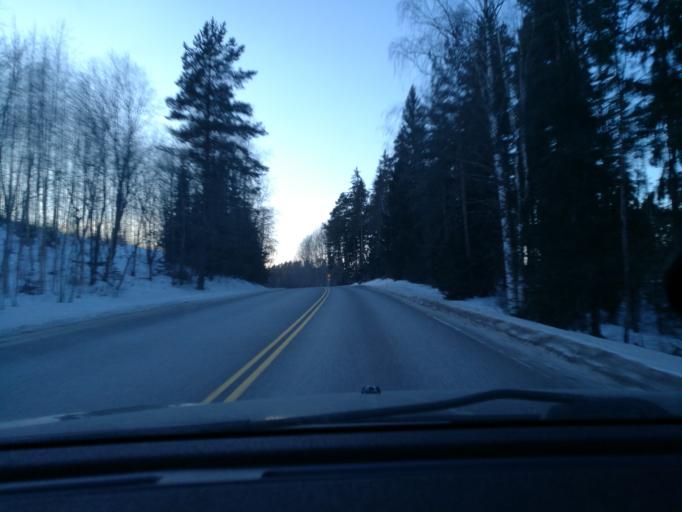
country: FI
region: Uusimaa
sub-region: Helsinki
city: Vihti
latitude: 60.4352
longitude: 24.4176
